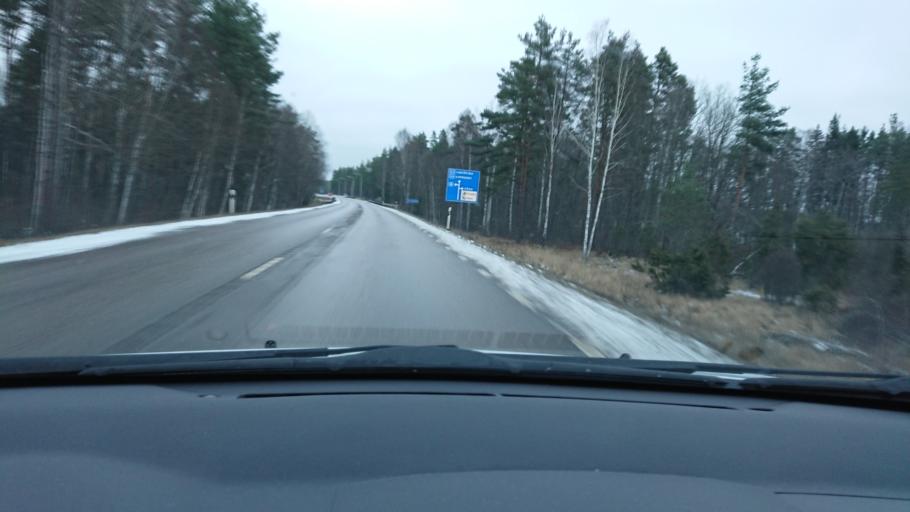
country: SE
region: Kalmar
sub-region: Hultsfreds Kommun
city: Hultsfred
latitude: 57.5138
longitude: 15.8399
